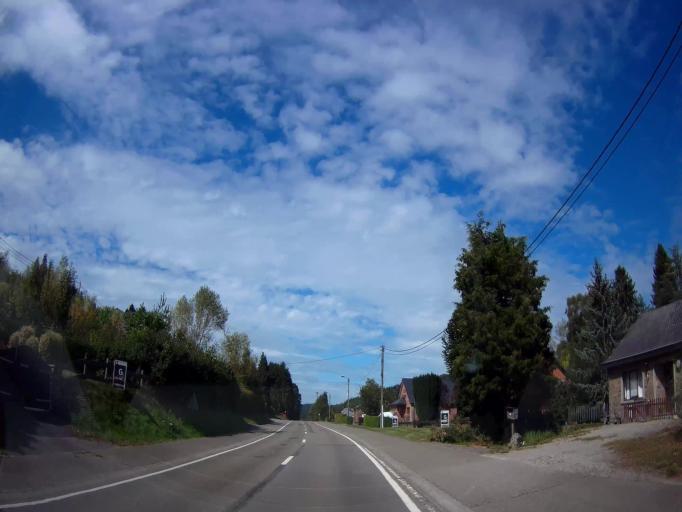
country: BE
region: Wallonia
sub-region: Province du Luxembourg
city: Rendeux
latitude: 50.2255
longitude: 5.5243
